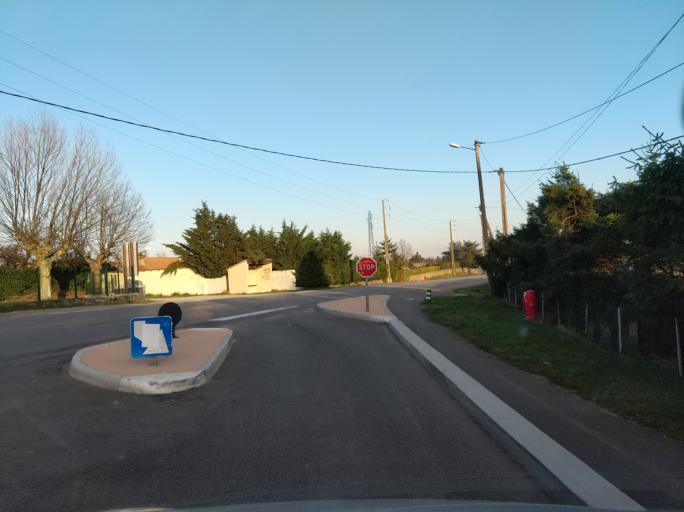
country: FR
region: Rhone-Alpes
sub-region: Departement de l'Ardeche
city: Boulieu-les-Annonay
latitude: 45.2710
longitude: 4.6739
